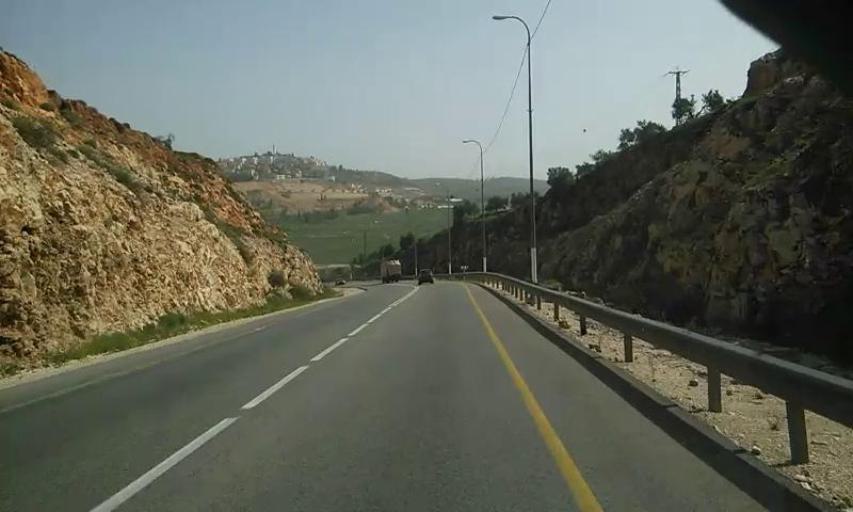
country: PS
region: West Bank
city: Turmus`ayya
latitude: 32.0489
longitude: 35.2896
